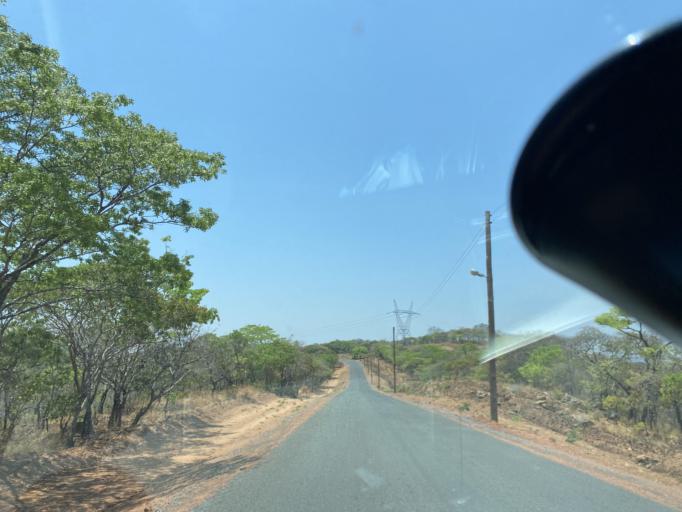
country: ZM
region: Lusaka
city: Kafue
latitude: -15.8649
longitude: 28.4548
